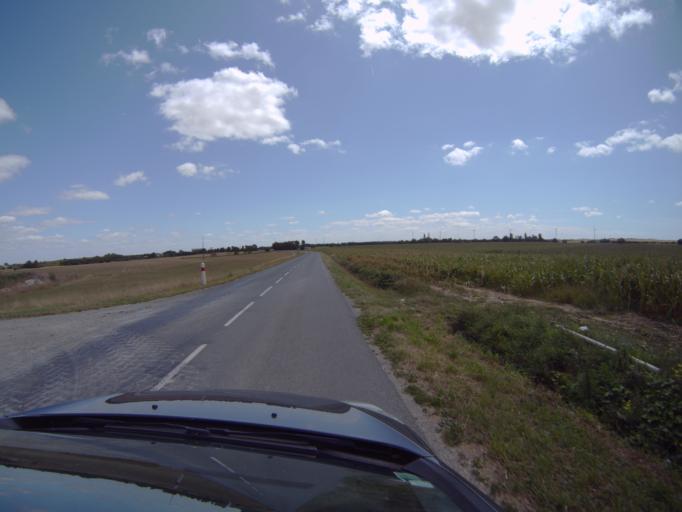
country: FR
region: Poitou-Charentes
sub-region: Departement de la Charente-Maritime
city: Saint-Jean-de-Liversay
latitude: 46.2639
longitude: -0.8723
